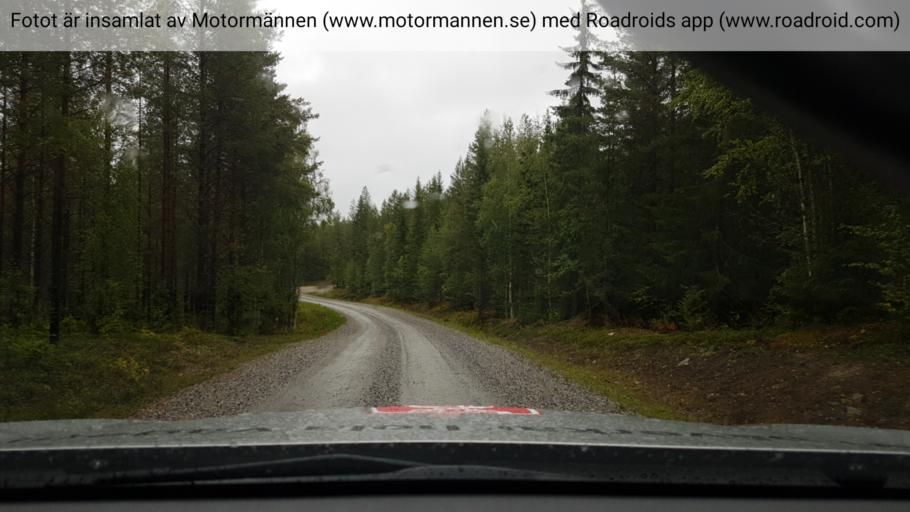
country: SE
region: Vaesterbotten
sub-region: Asele Kommun
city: Asele
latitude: 63.9967
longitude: 17.6074
